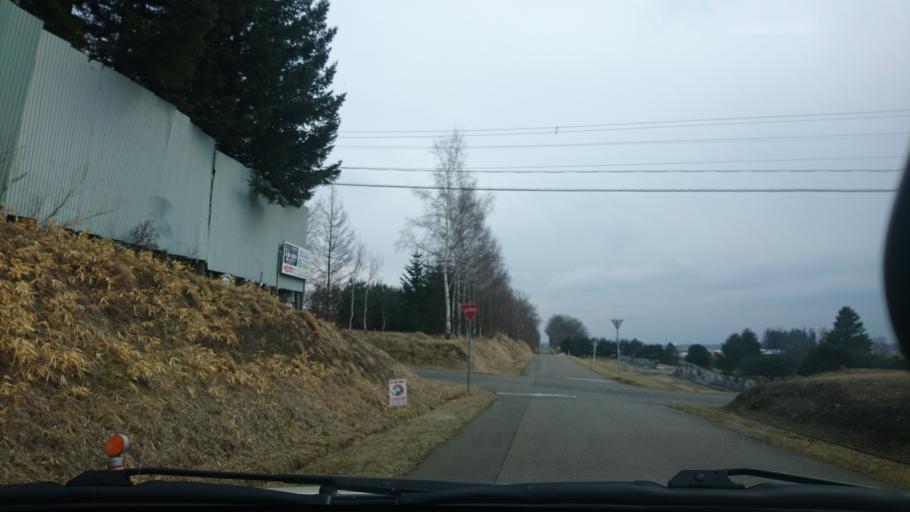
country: JP
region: Hokkaido
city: Otofuke
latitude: 43.0184
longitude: 143.2130
